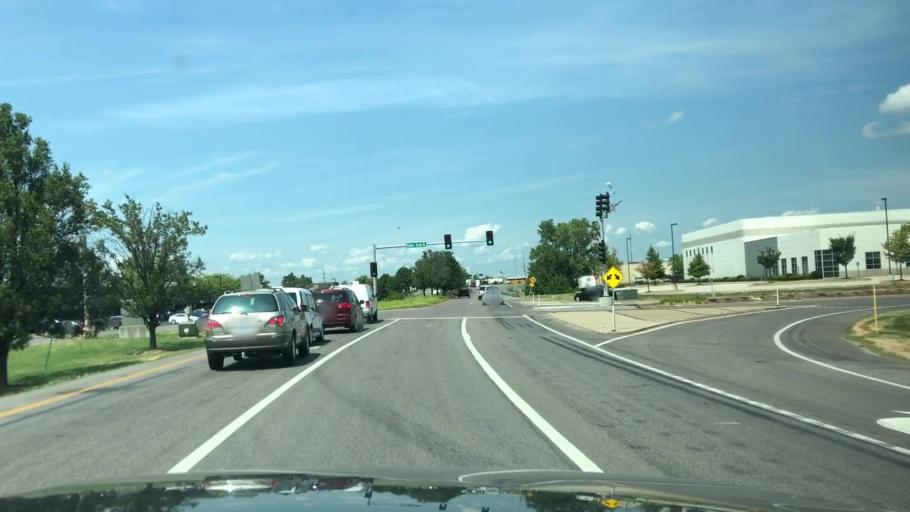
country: US
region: Missouri
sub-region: Saint Charles County
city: Saint Charles
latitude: 38.7755
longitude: -90.4605
